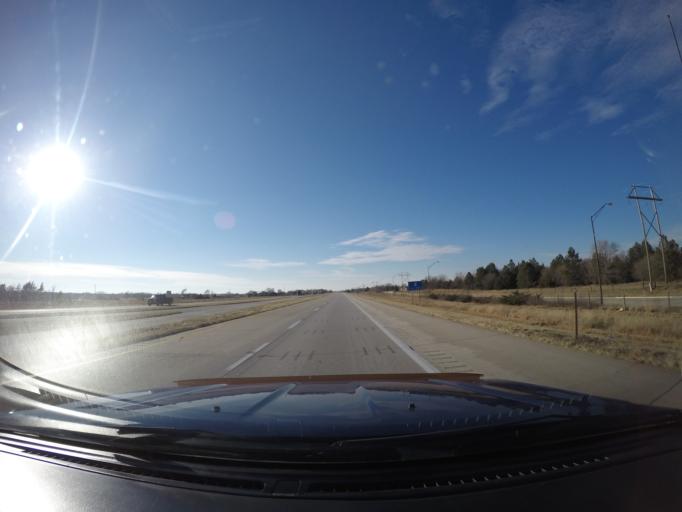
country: US
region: Nebraska
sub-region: Buffalo County
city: Kearney
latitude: 40.6699
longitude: -99.0493
